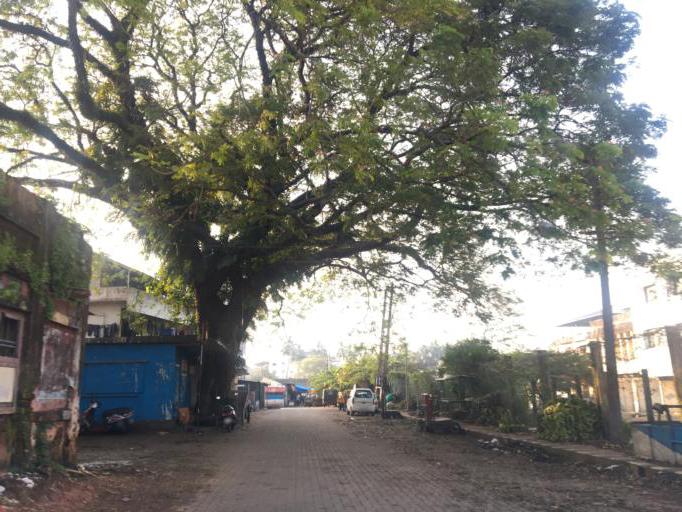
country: IN
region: Kerala
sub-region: Ernakulam
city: Cochin
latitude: 9.9828
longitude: 76.2770
